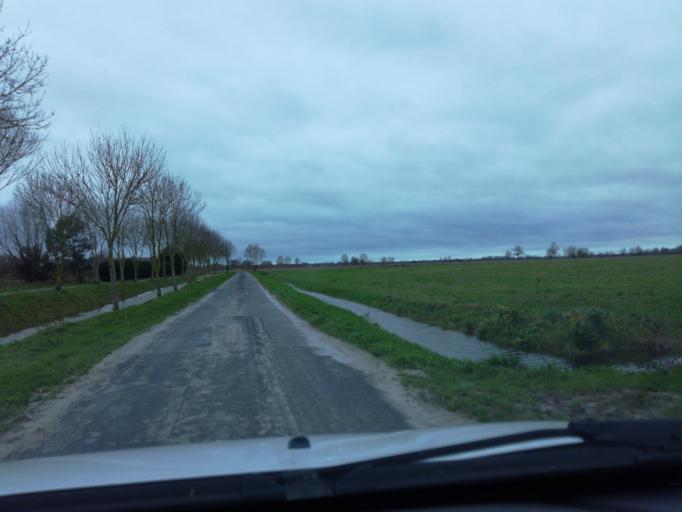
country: FR
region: Brittany
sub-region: Departement d'Ille-et-Vilaine
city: Dol-de-Bretagne
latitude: 48.5675
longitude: -1.7272
